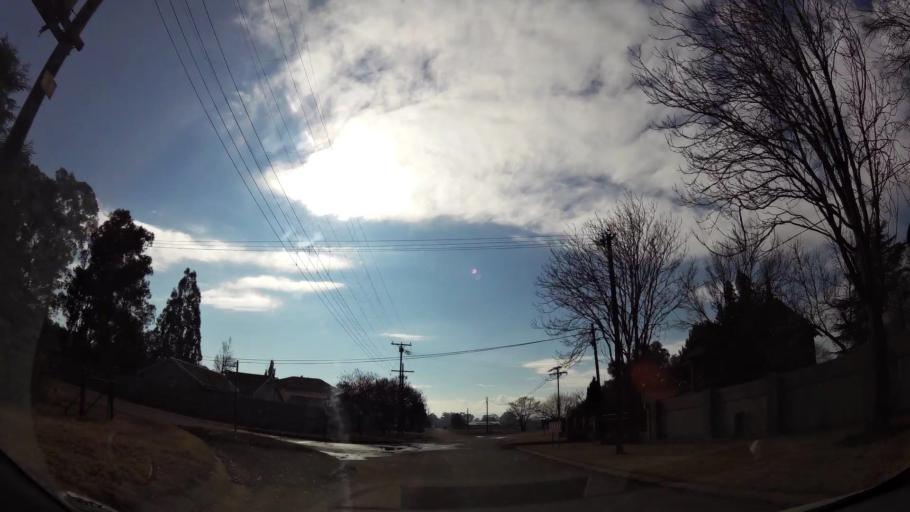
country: ZA
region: Gauteng
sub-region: Sedibeng District Municipality
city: Meyerton
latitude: -26.5521
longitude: 28.0553
